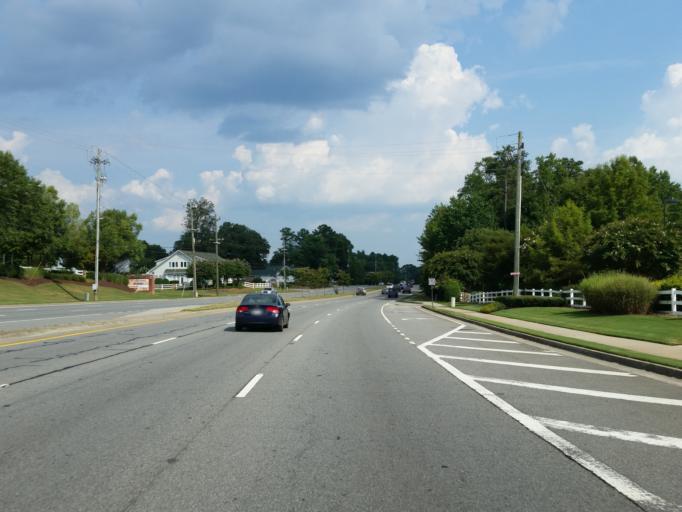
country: US
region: Georgia
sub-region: Fulton County
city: Roswell
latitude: 34.0579
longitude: -84.3806
